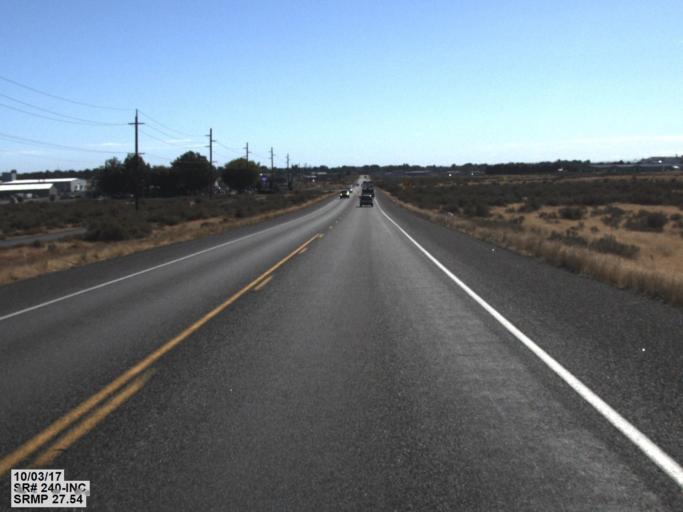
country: US
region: Washington
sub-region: Benton County
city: Richland
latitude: 46.3204
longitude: -119.3062
